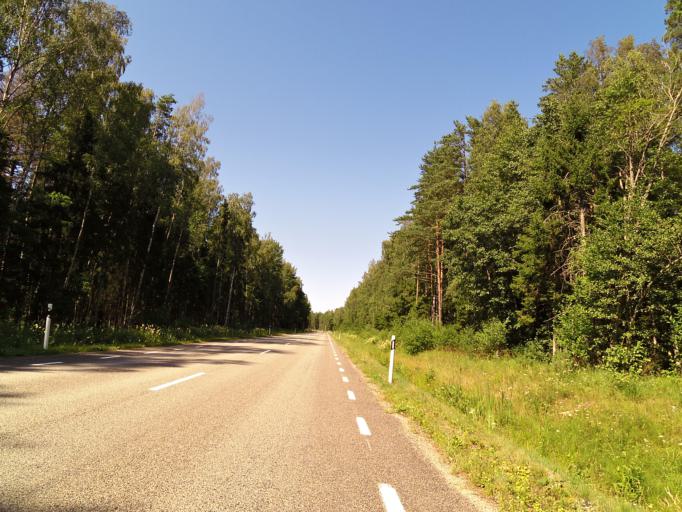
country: EE
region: Hiiumaa
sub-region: Kaerdla linn
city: Kardla
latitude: 58.8024
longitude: 22.4849
